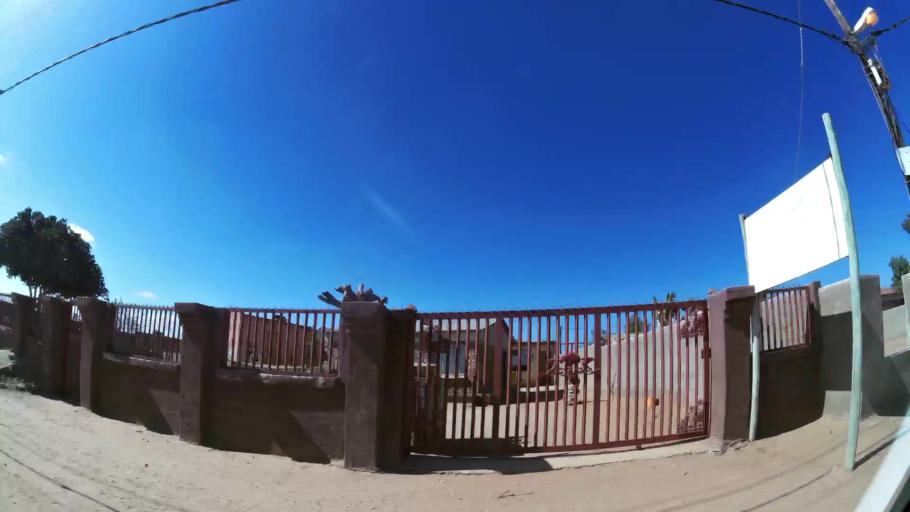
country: ZA
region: Limpopo
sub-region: Capricorn District Municipality
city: Polokwane
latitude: -23.8807
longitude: 29.4042
